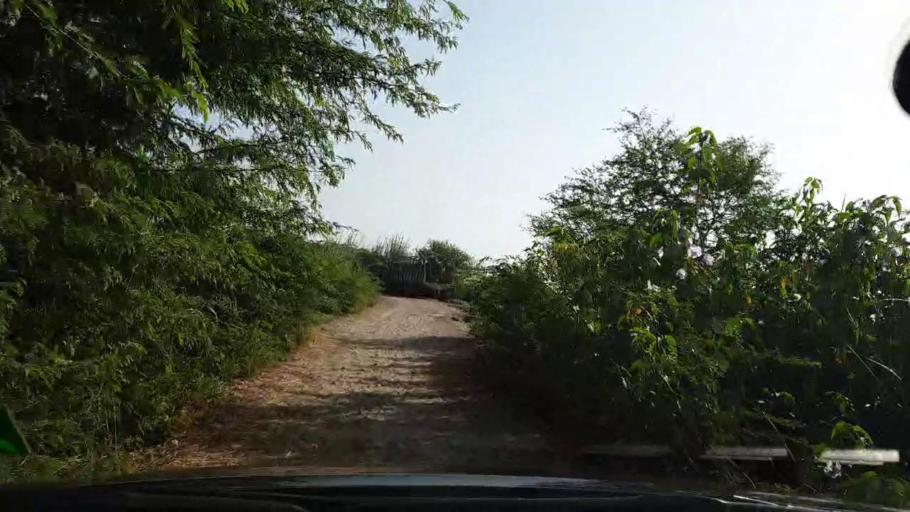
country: PK
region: Sindh
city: Tando Bago
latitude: 24.6534
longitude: 69.0404
